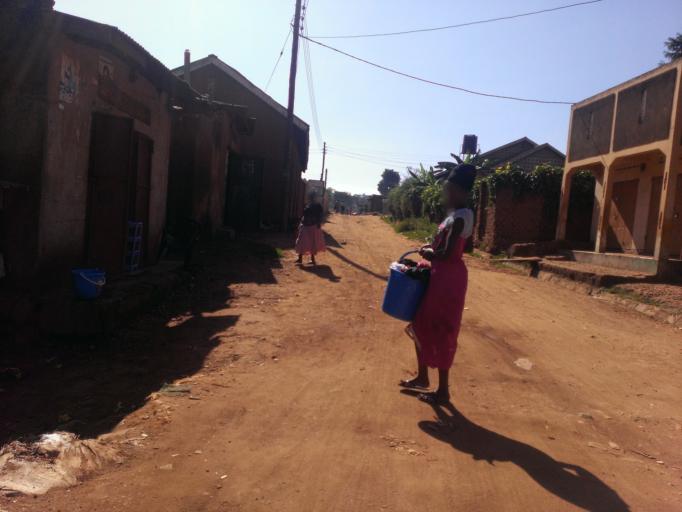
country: UG
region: Central Region
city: Kampala Central Division
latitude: 0.3280
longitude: 32.5593
